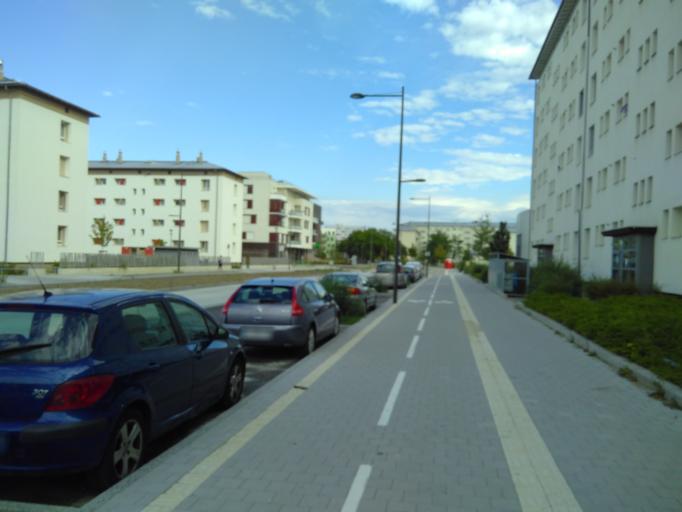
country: FR
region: Alsace
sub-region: Departement du Bas-Rhin
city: Strasbourg
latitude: 48.5485
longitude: 7.7546
